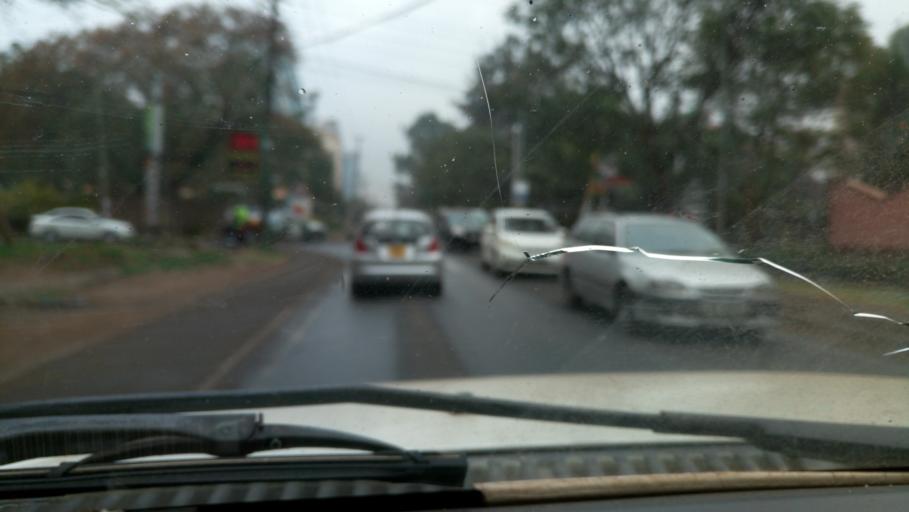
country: KE
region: Nairobi Area
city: Nairobi
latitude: -1.2890
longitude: 36.7907
